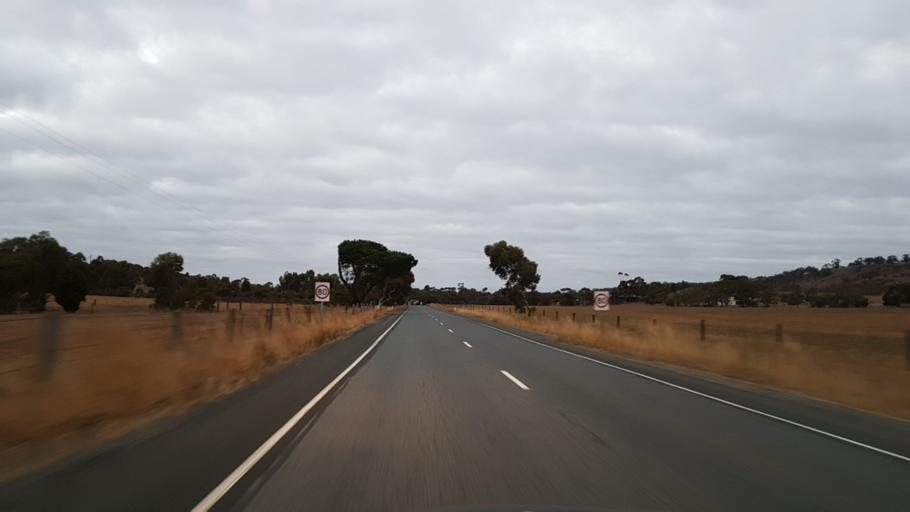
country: AU
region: South Australia
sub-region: Mount Barker
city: Callington
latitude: -35.0627
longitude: 139.0121
